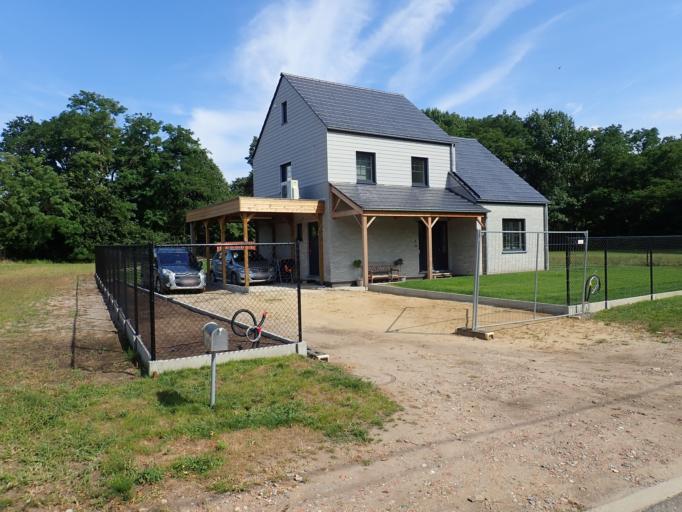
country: BE
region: Flanders
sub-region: Provincie Vlaams-Brabant
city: Keerbergen
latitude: 50.9929
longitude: 4.6436
